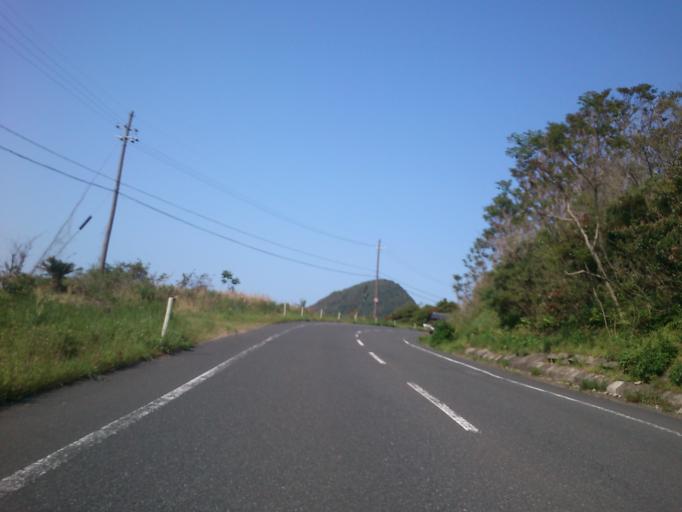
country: JP
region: Kyoto
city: Miyazu
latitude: 35.7652
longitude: 135.2112
